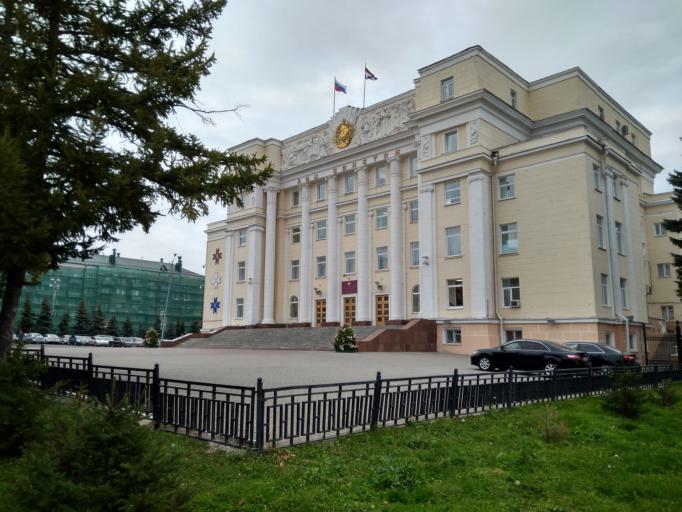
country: RU
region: Mordoviya
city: Saransk
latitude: 54.1799
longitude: 45.1880
